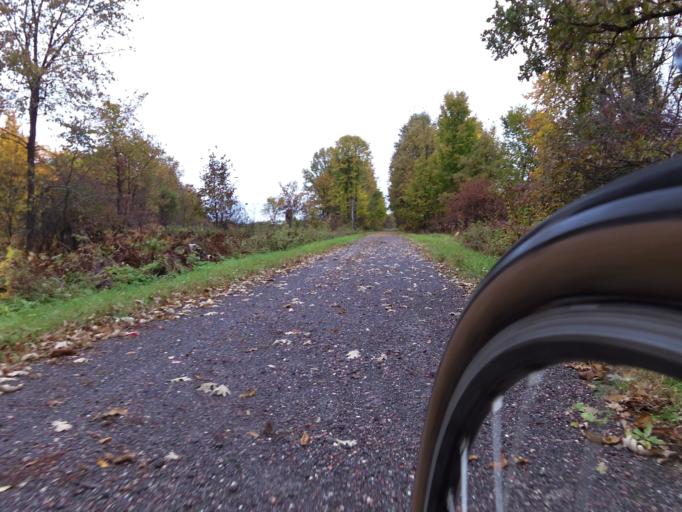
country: CA
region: Quebec
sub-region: Outaouais
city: Shawville
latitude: 45.6964
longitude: -76.5775
